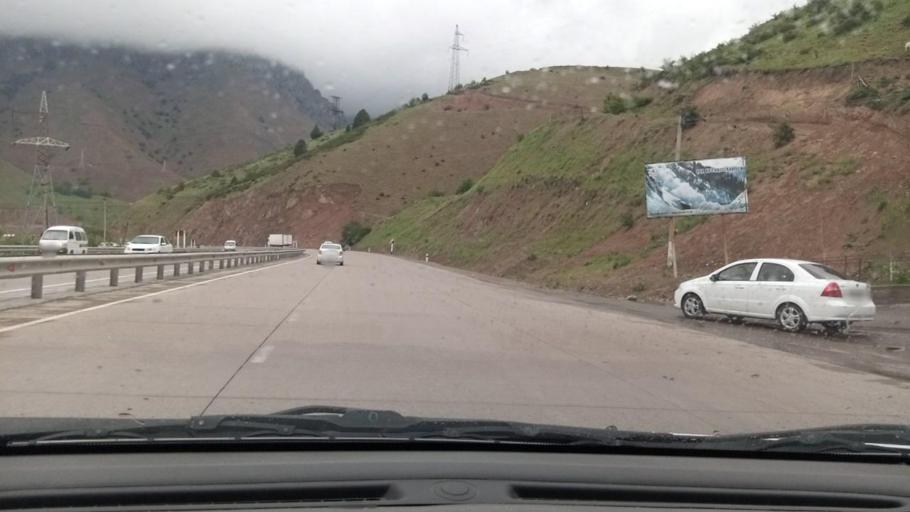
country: UZ
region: Toshkent
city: Angren
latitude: 41.1484
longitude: 70.4463
